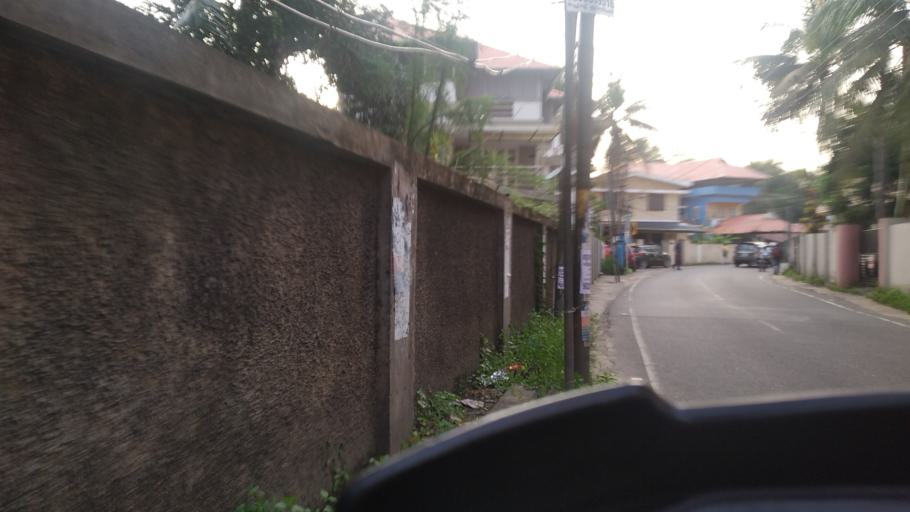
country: IN
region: Kerala
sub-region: Ernakulam
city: Elur
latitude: 10.0239
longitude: 76.2997
